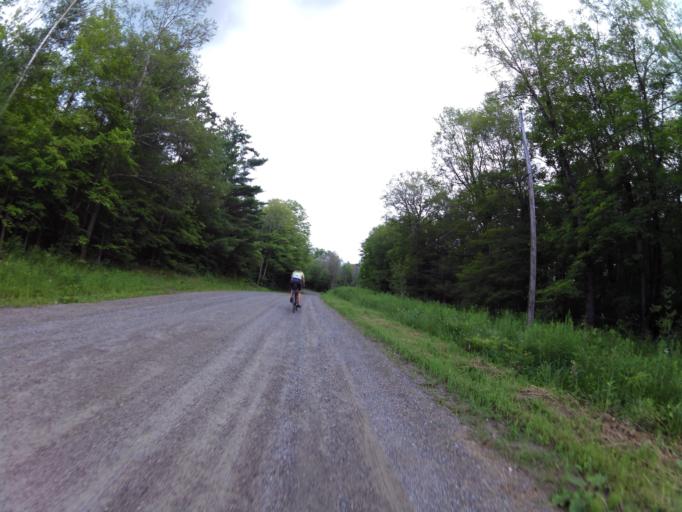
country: CA
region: Ontario
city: Renfrew
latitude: 45.1209
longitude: -76.6253
